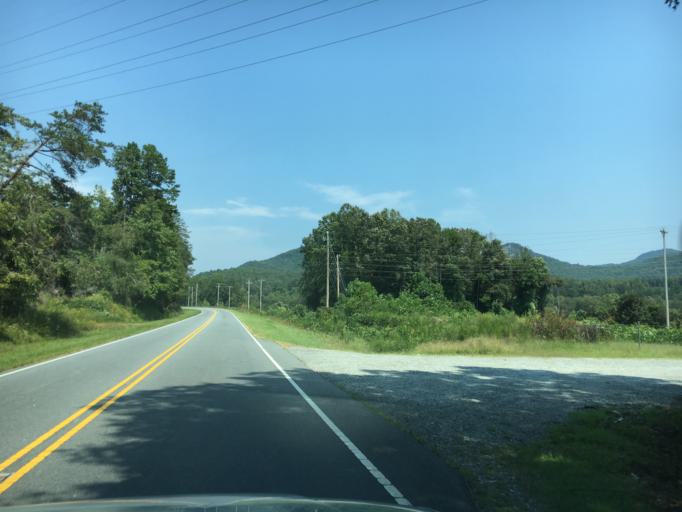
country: US
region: North Carolina
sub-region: Rutherford County
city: Rutherfordton
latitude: 35.5103
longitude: -81.9738
